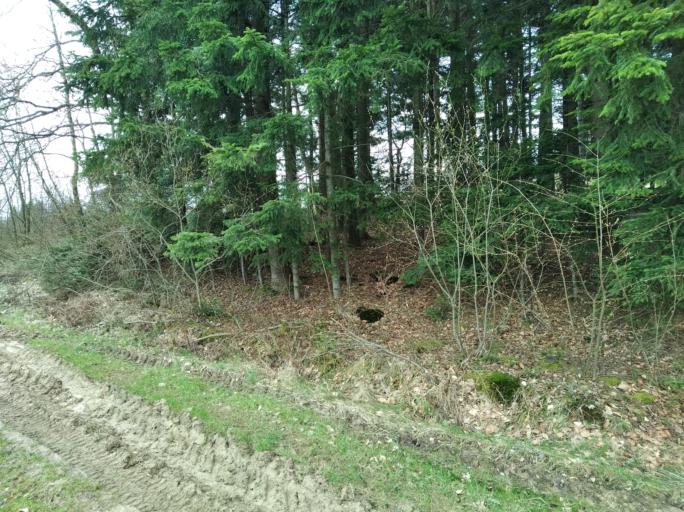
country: PL
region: Subcarpathian Voivodeship
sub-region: Powiat strzyzowski
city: Wysoka Strzyzowska
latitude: 49.8059
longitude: 21.7676
